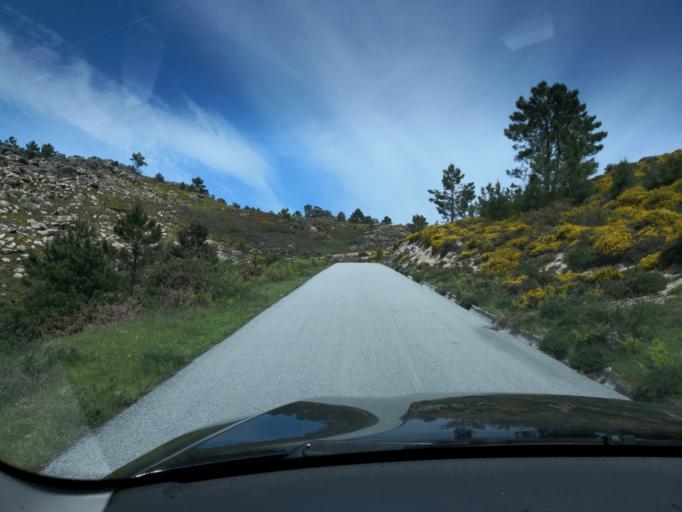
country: PT
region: Vila Real
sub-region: Vila Real
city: Vila Real
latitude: 41.3232
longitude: -7.7902
